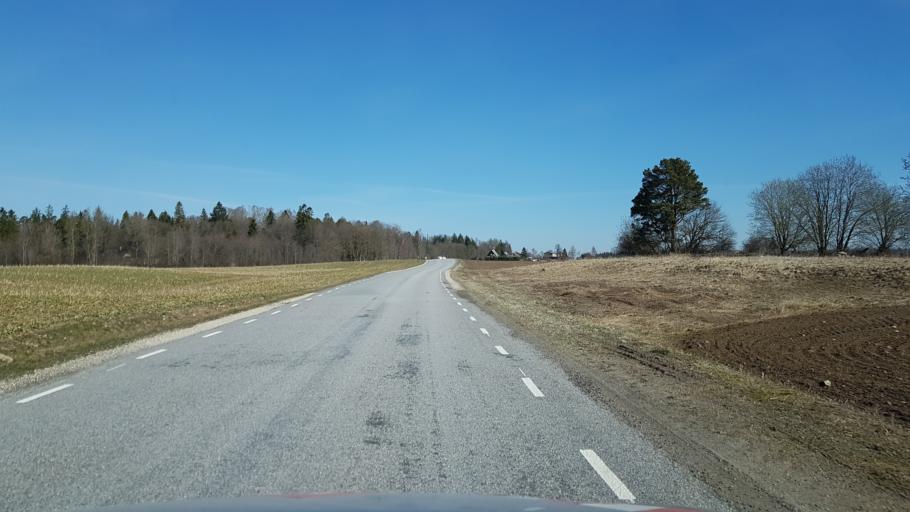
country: EE
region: Laeaene-Virumaa
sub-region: Vinni vald
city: Vinni
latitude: 59.2603
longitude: 26.3616
